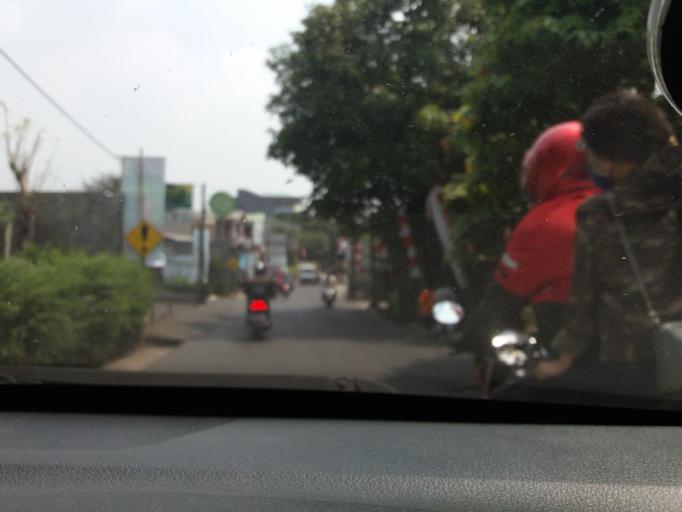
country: ID
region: West Java
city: Depok
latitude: -6.3302
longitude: 106.8267
